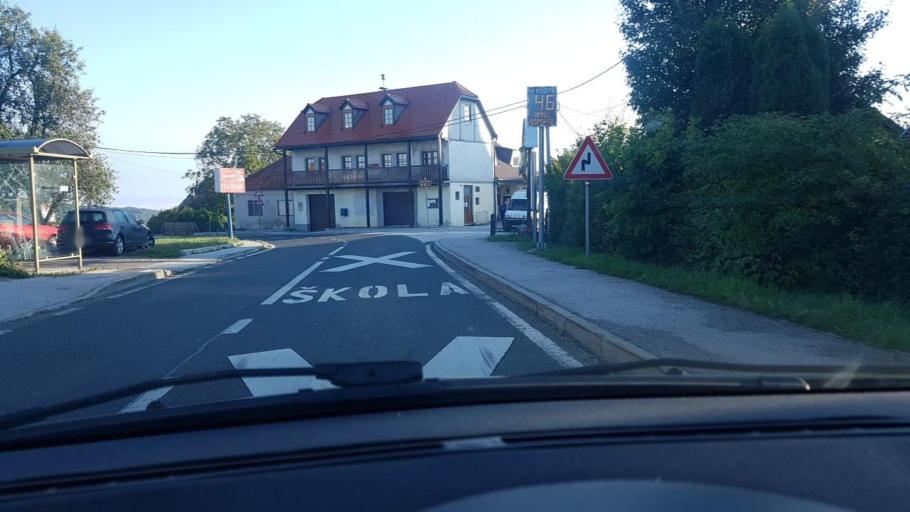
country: HR
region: Krapinsko-Zagorska
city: Marija Bistrica
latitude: 45.9705
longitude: 16.0983
